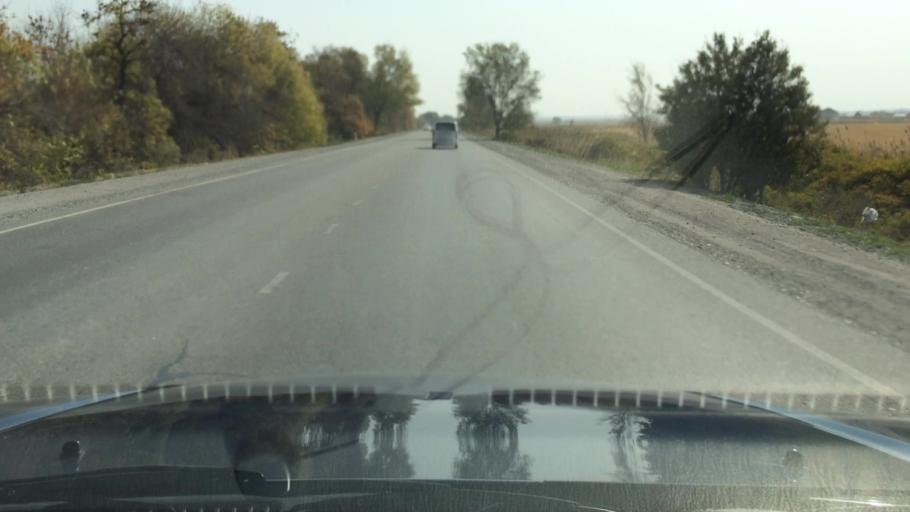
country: KG
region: Chuy
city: Lebedinovka
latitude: 42.9280
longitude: 74.6957
